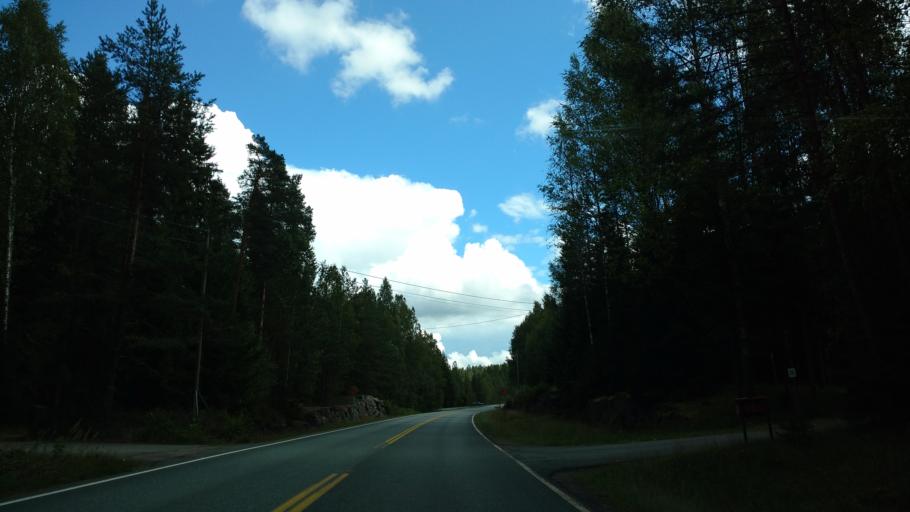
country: FI
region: Varsinais-Suomi
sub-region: Salo
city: Kisko
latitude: 60.2389
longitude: 23.5747
